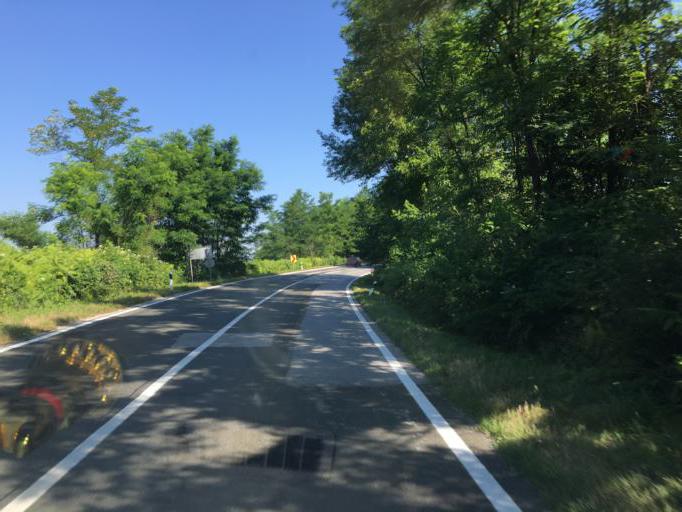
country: HR
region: Karlovacka
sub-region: Grad Karlovac
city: Slunj
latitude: 45.2540
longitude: 15.5536
